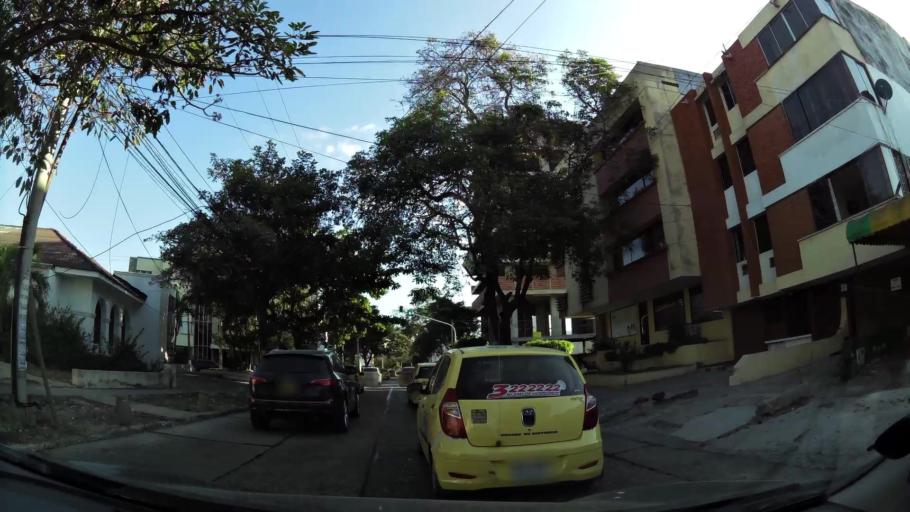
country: CO
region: Atlantico
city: Barranquilla
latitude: 10.9967
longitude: -74.8068
